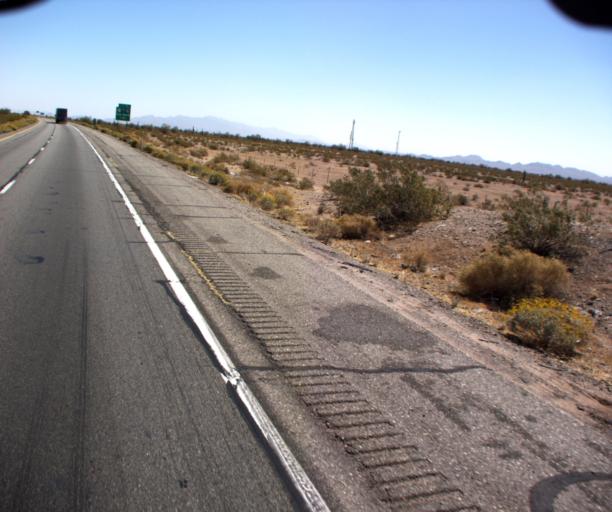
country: US
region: Arizona
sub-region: Maricopa County
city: Buckeye
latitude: 33.4315
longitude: -112.6470
